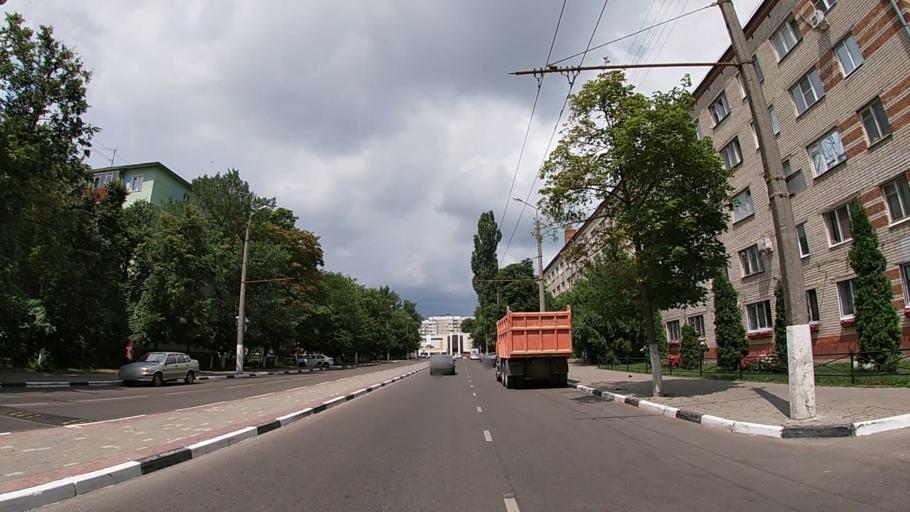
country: RU
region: Belgorod
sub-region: Belgorodskiy Rayon
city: Belgorod
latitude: 50.6113
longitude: 36.5914
